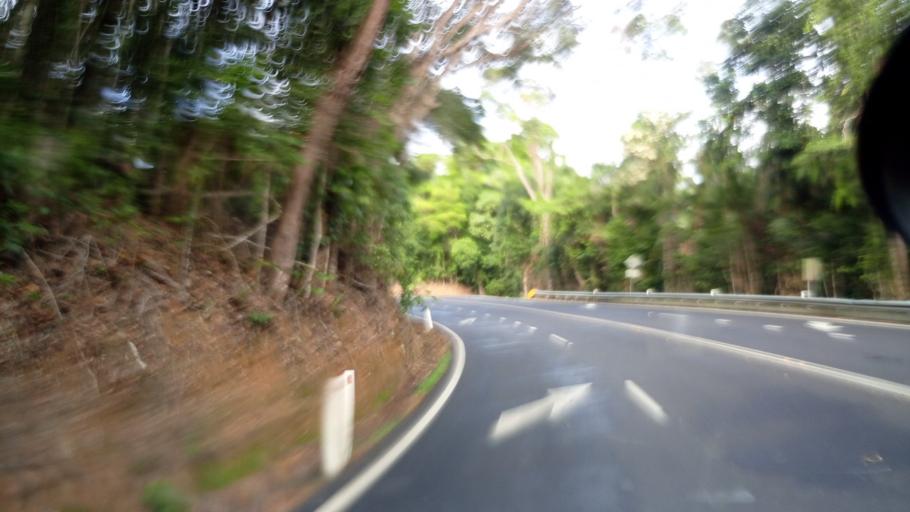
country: AU
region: Queensland
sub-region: Tablelands
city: Kuranda
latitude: -16.8315
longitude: 145.6676
